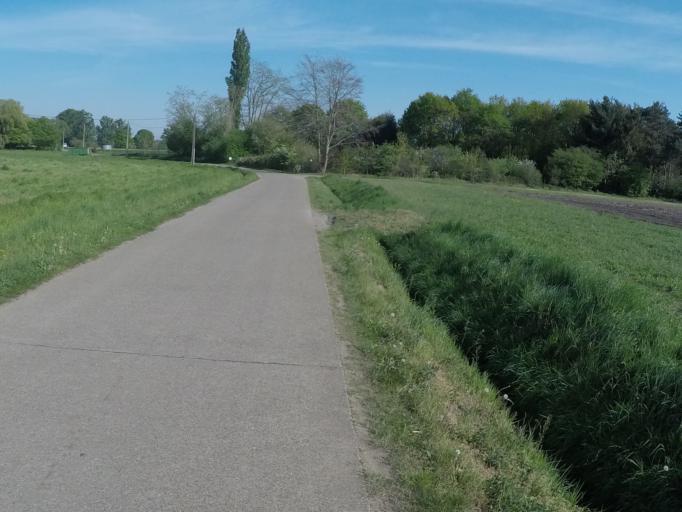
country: BE
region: Flanders
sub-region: Provincie Antwerpen
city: Nijlen
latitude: 51.1577
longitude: 4.6946
